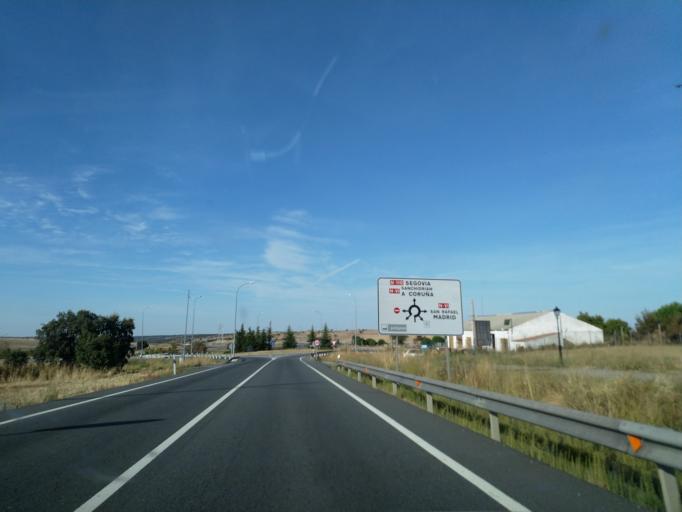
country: ES
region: Castille and Leon
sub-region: Provincia de Segovia
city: Villacastin
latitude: 40.7813
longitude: -4.4216
